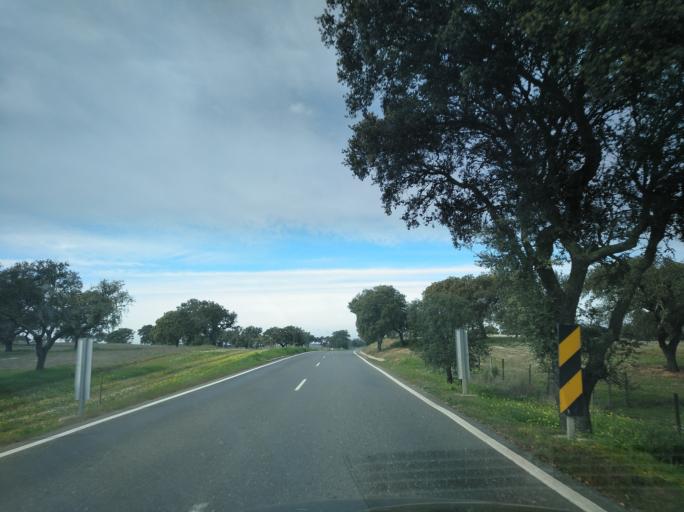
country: PT
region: Beja
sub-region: Mertola
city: Mertola
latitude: 37.7639
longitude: -7.8185
